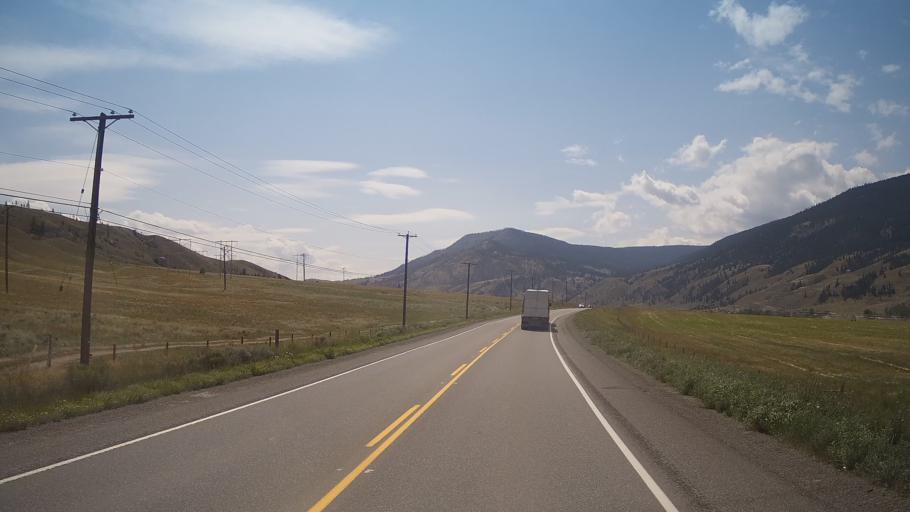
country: CA
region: British Columbia
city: Cache Creek
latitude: 50.8590
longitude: -121.3858
